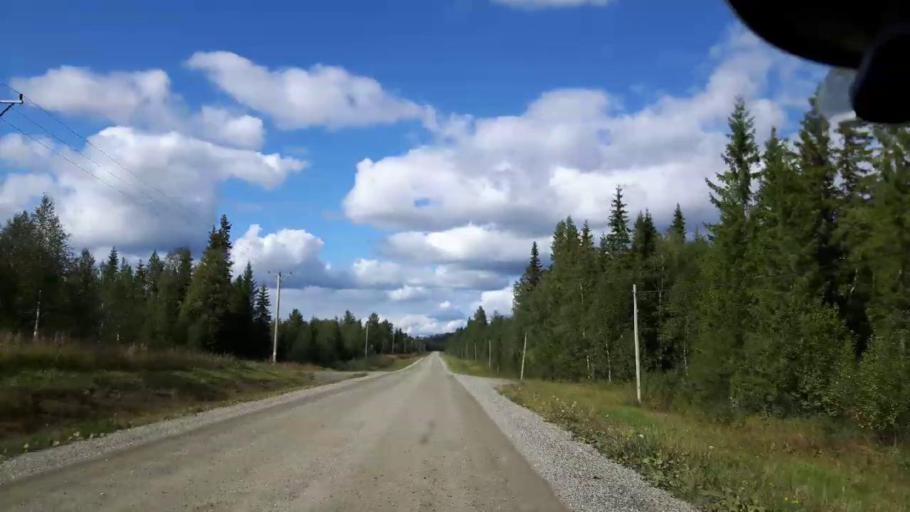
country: SE
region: Jaemtland
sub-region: Stroemsunds Kommun
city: Stroemsund
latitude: 63.3173
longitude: 15.5877
